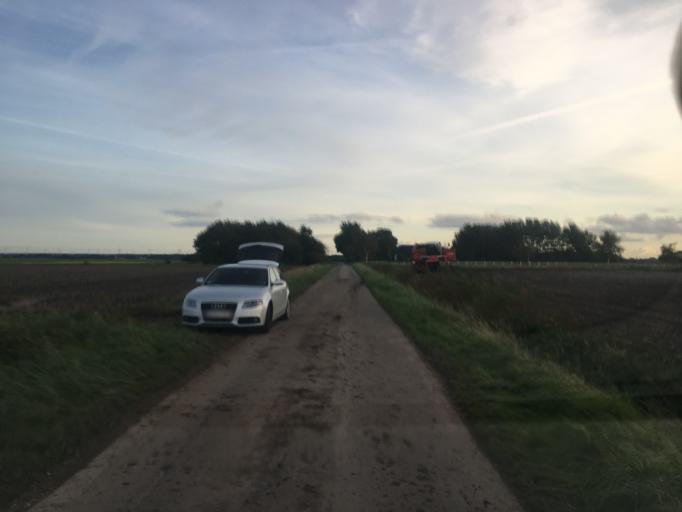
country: DK
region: South Denmark
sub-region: Tonder Kommune
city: Tonder
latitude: 54.9733
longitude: 8.9042
